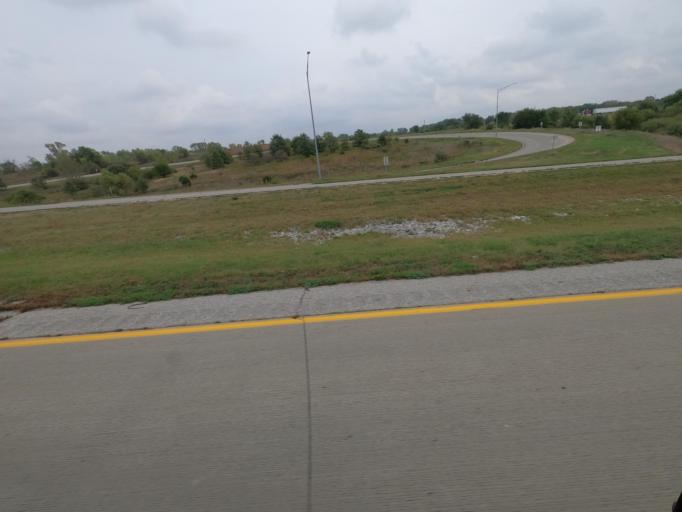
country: US
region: Iowa
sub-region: Wapello County
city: Eddyville
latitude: 41.1488
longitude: -92.6232
